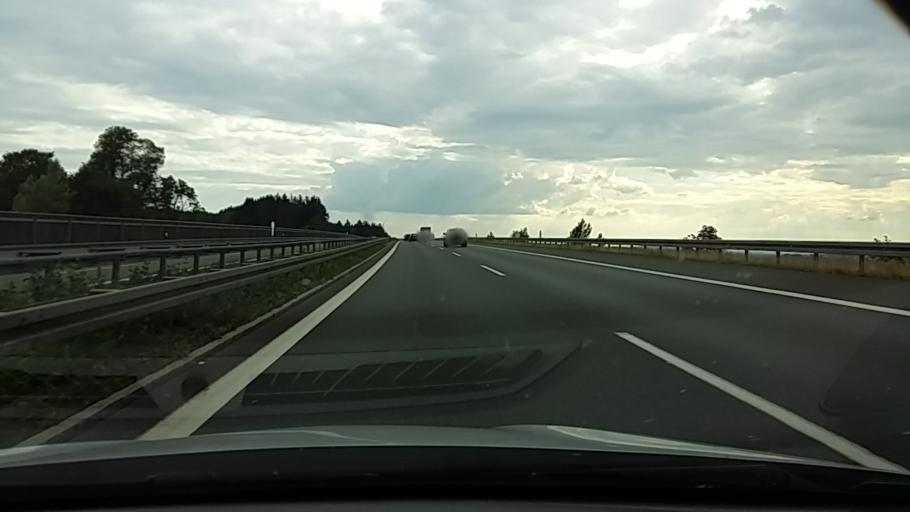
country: DE
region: Bavaria
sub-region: Upper Palatinate
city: Vohenstrauss
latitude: 49.5937
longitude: 12.3058
